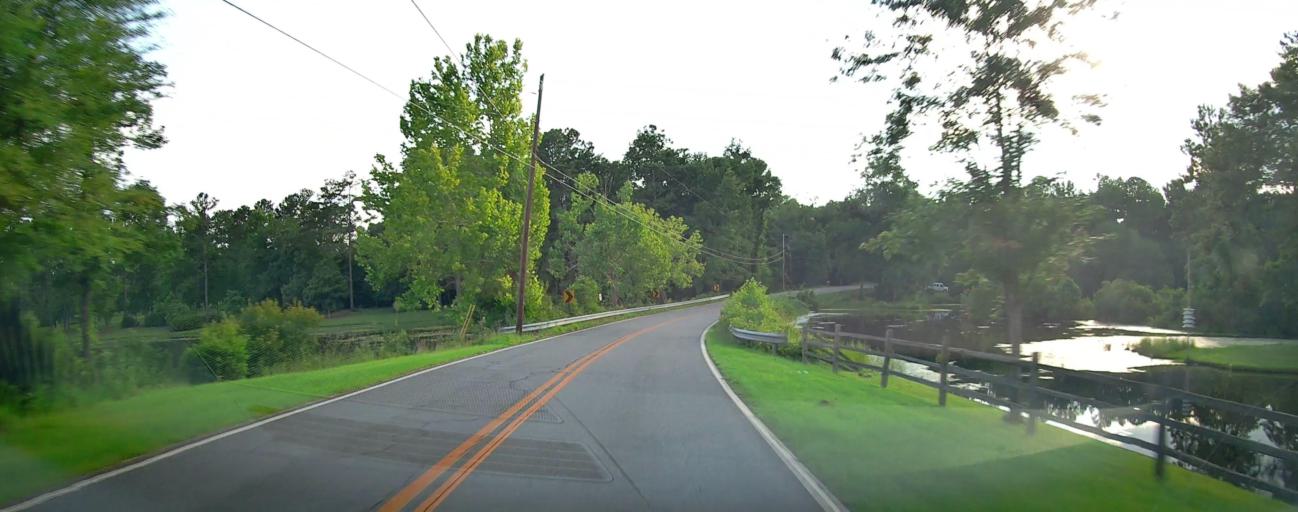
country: US
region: Georgia
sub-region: Peach County
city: Byron
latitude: 32.7168
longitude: -83.7508
